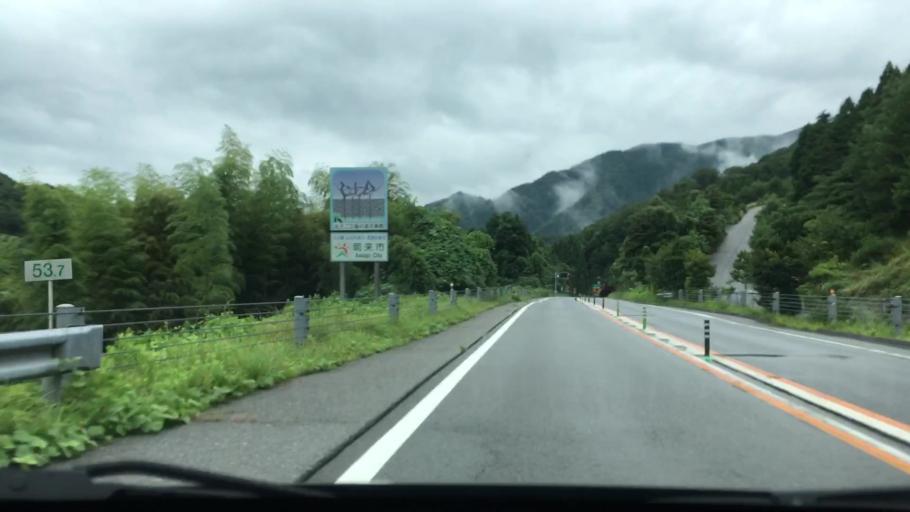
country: JP
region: Hyogo
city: Toyooka
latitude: 35.2446
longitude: 134.7892
